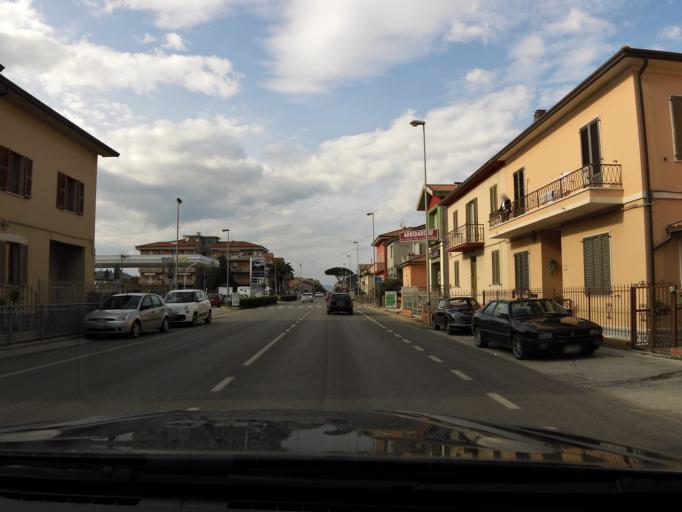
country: IT
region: The Marches
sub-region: Provincia di Macerata
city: Porto Potenza Picena
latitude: 43.3533
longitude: 13.6999
